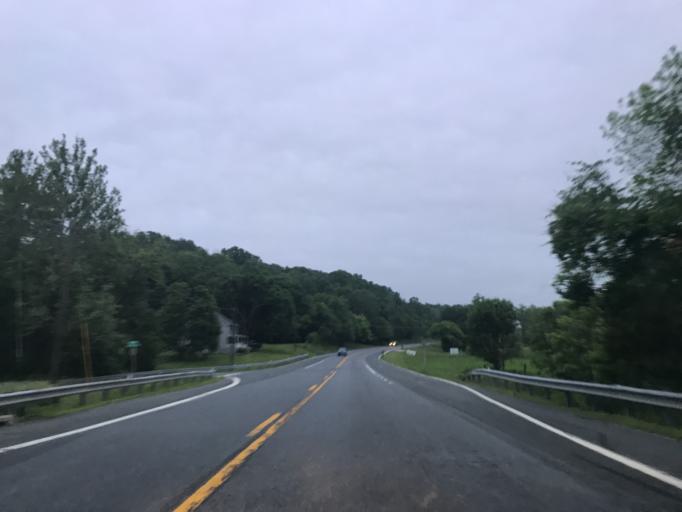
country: US
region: Maryland
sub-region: Frederick County
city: Linganore
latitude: 39.4476
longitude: -77.2483
